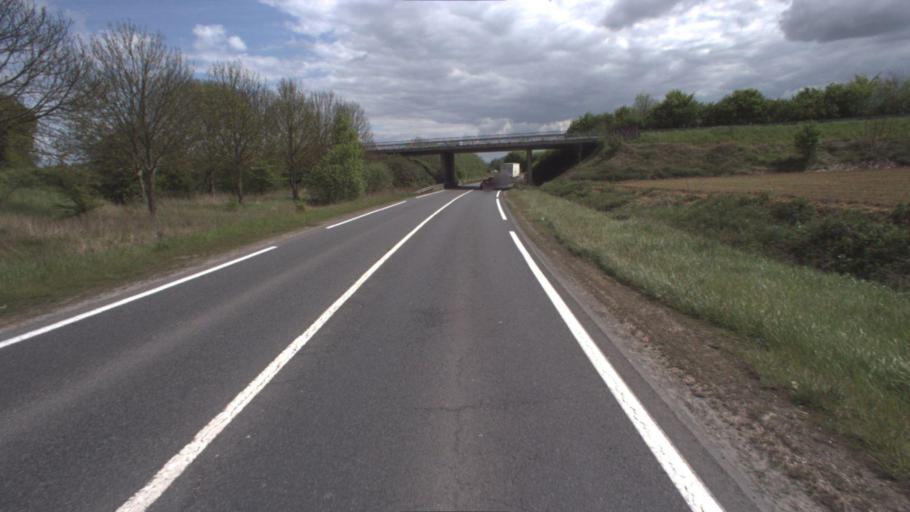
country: FR
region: Ile-de-France
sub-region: Departement de Seine-et-Marne
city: Cregy-les-Meaux
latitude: 48.9903
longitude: 2.8675
